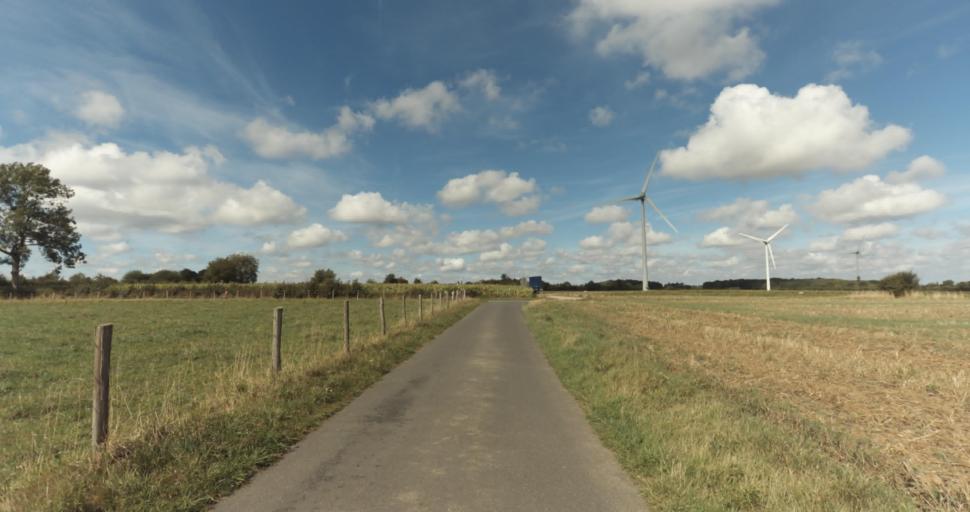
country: FR
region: Lower Normandy
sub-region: Departement du Calvados
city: La Vespiere
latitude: 48.9605
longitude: 0.3706
